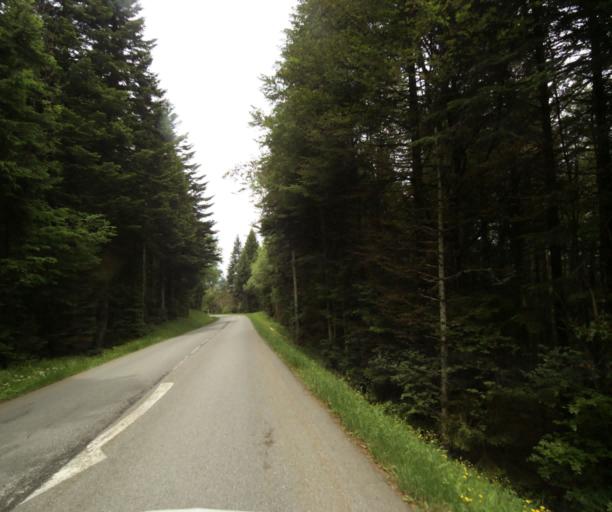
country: FR
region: Rhone-Alpes
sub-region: Departement de la Haute-Savoie
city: Perrignier
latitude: 46.2635
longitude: 6.4472
